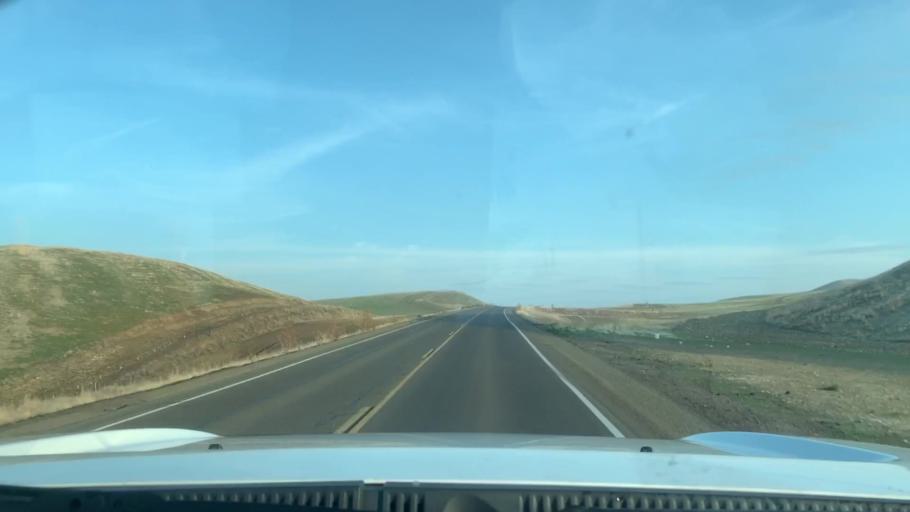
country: US
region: California
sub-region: Kings County
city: Avenal
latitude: 35.8506
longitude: -120.0803
